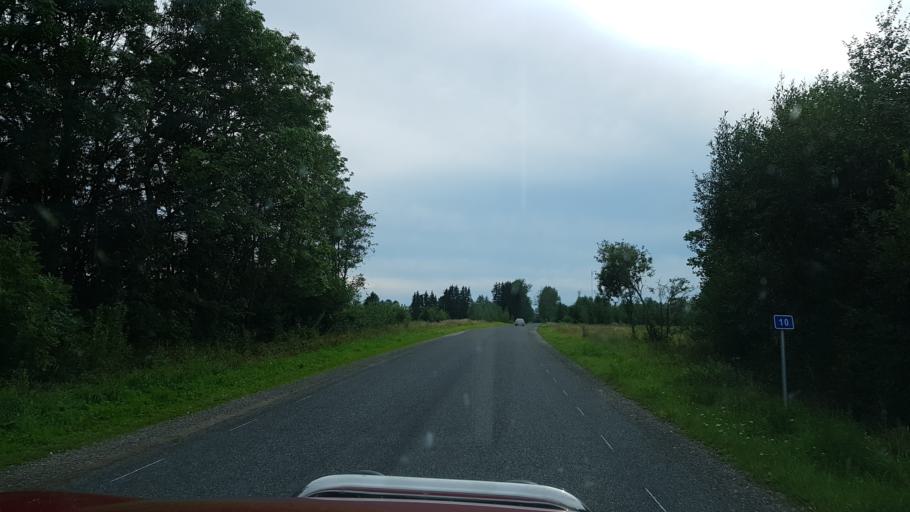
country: EE
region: Laeaene
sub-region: Lihula vald
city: Lihula
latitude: 58.8917
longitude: 23.8832
